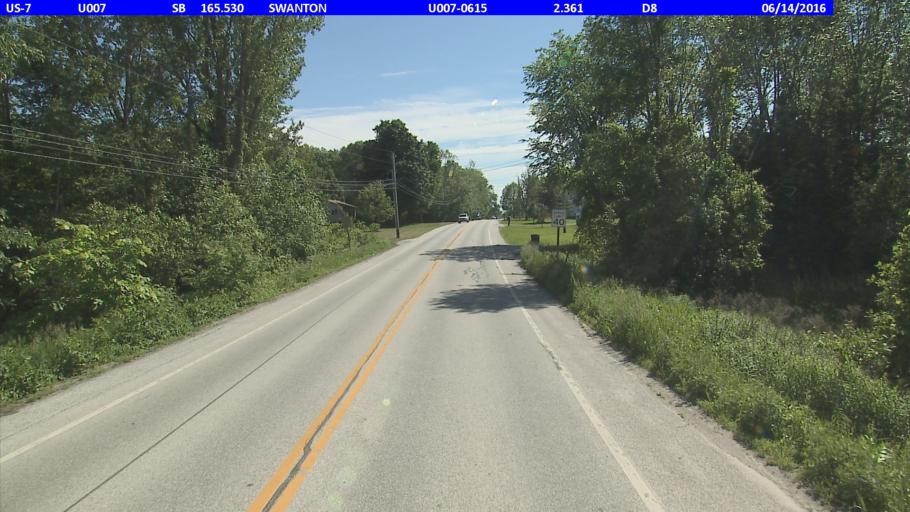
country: US
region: Vermont
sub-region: Franklin County
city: Swanton
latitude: 44.8811
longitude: -73.0959
